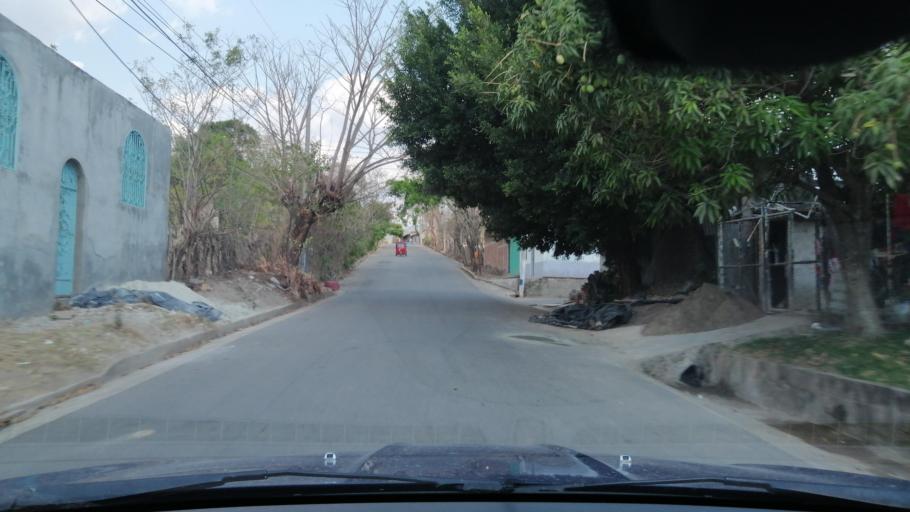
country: SV
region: Santa Ana
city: Metapan
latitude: 14.3294
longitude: -89.4312
